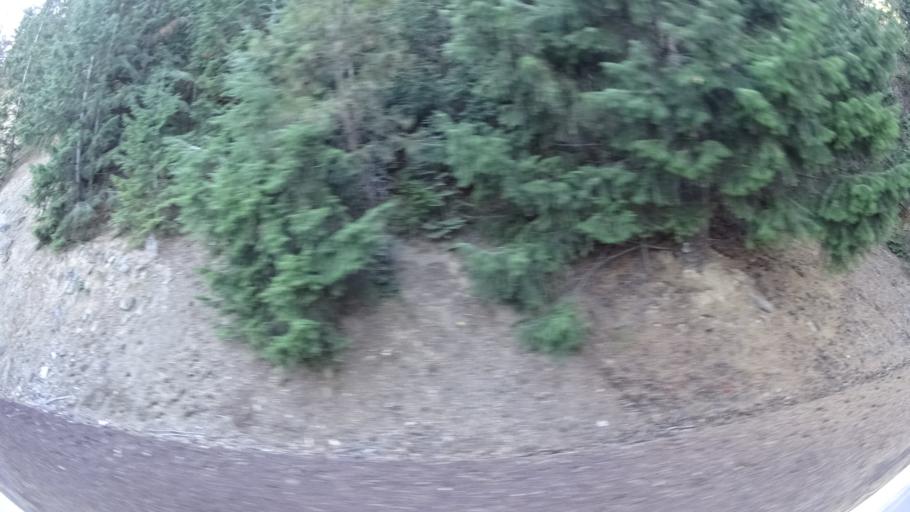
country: US
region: California
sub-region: Siskiyou County
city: Weed
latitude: 41.4436
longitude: -122.6459
